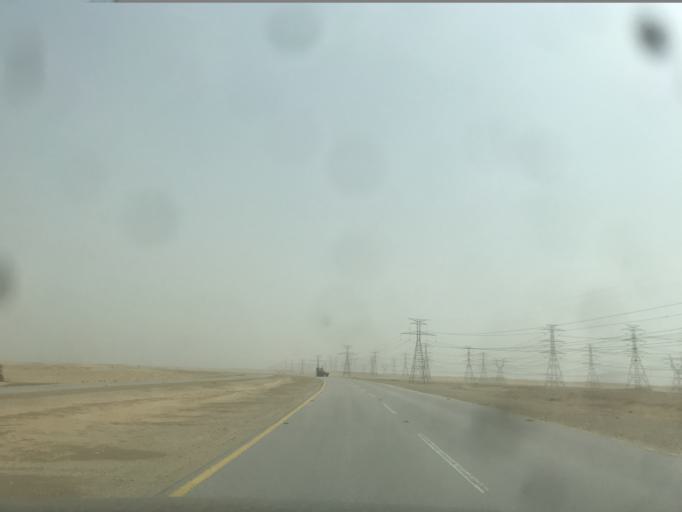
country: SA
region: Eastern Province
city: Abqaiq
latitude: 25.9138
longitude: 49.7961
